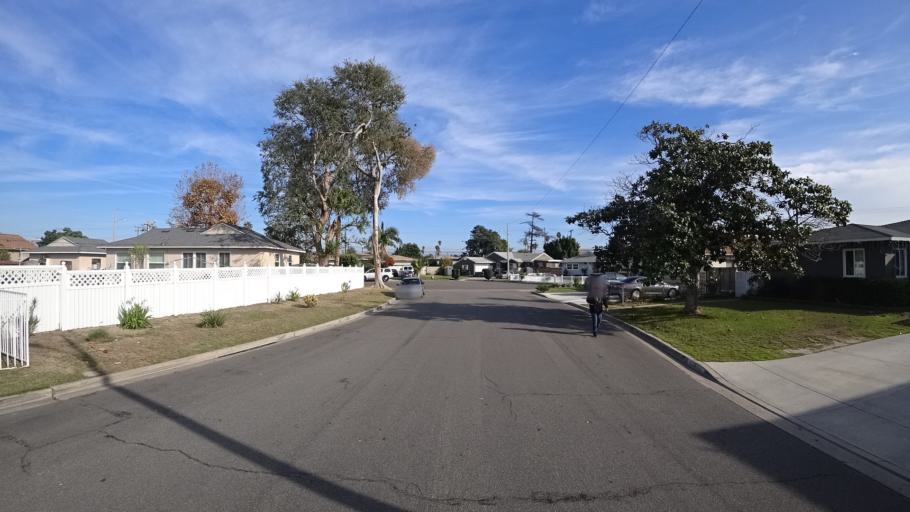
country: US
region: California
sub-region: Orange County
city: Garden Grove
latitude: 33.7694
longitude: -117.9044
